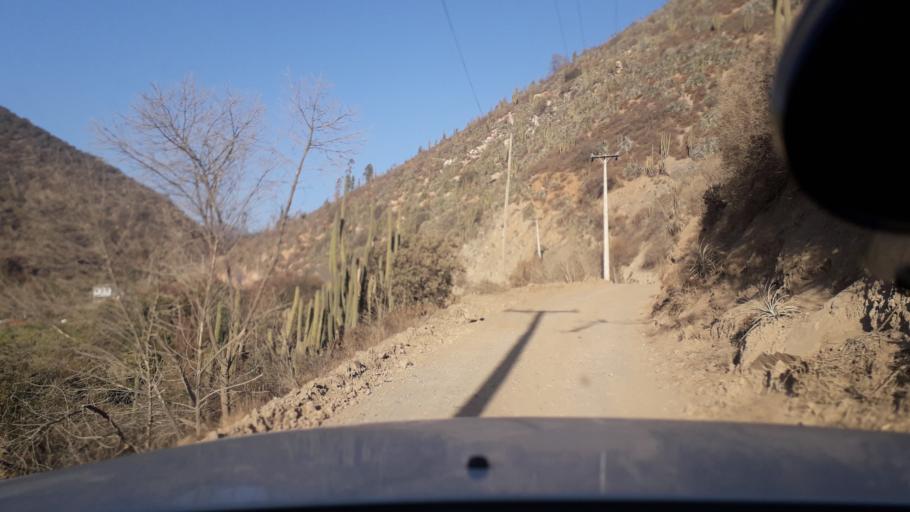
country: CL
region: Valparaiso
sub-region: Provincia de Marga Marga
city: Limache
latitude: -33.0524
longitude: -71.0814
